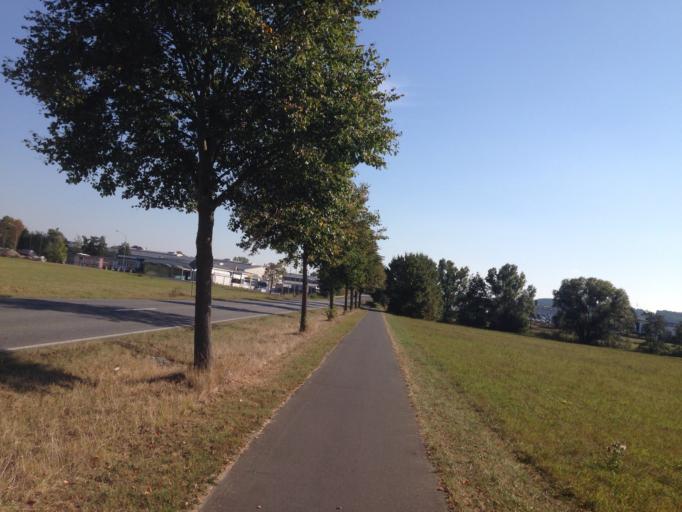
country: DE
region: Hesse
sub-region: Regierungsbezirk Giessen
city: Giessen
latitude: 50.5449
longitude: 8.7048
